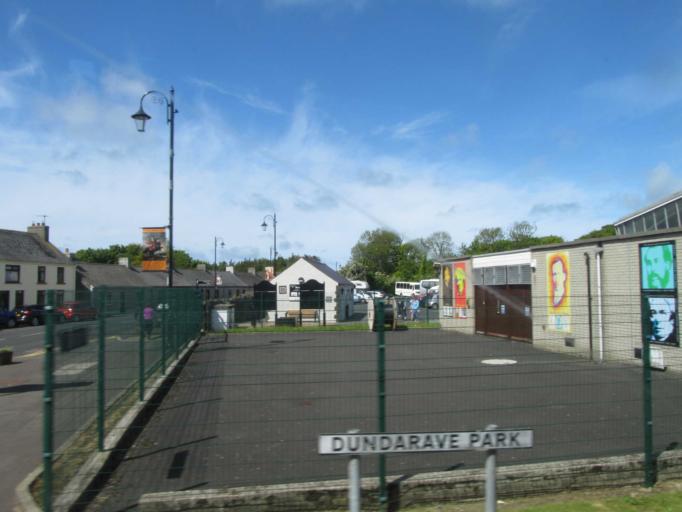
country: GB
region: Northern Ireland
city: Bushmills
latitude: 55.2069
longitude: -6.5236
